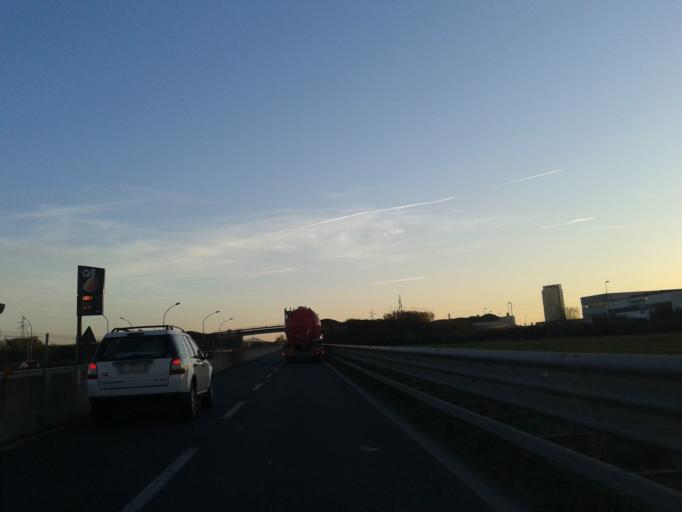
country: IT
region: Tuscany
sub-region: Provincia di Livorno
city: Livorno
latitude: 43.5685
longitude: 10.3473
